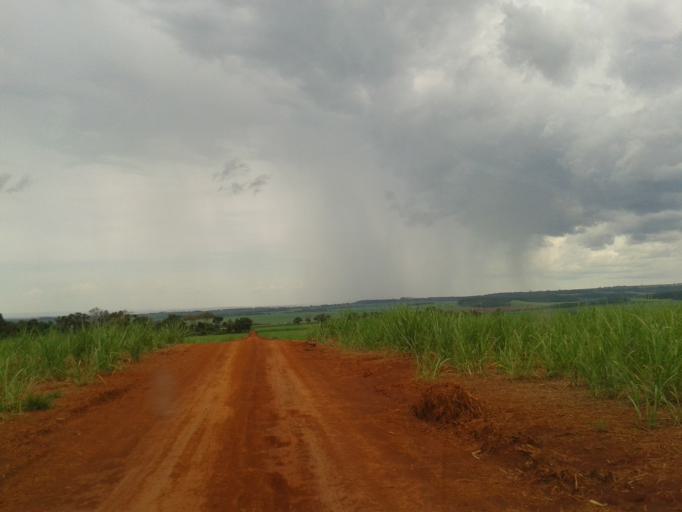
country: BR
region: Minas Gerais
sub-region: Centralina
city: Centralina
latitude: -18.6661
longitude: -49.2595
